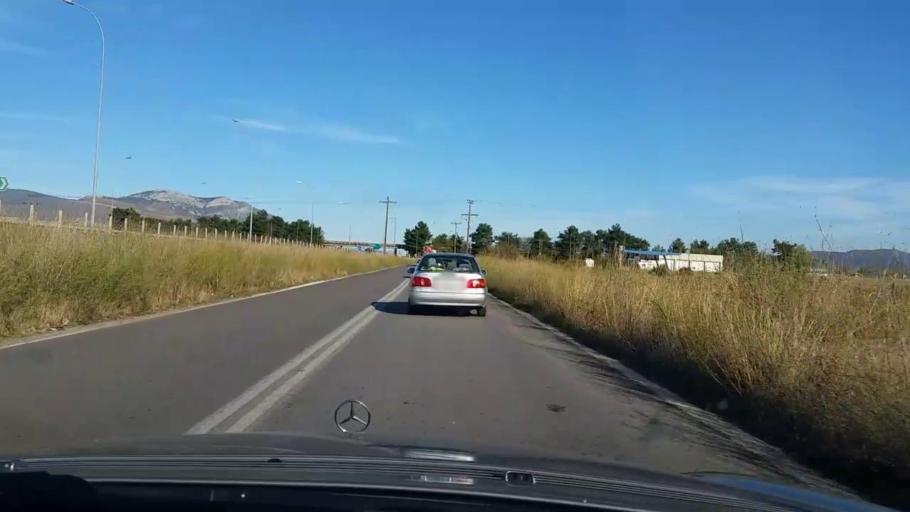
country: GR
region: Central Greece
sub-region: Nomos Voiotias
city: Thivai
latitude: 38.3646
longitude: 23.3191
